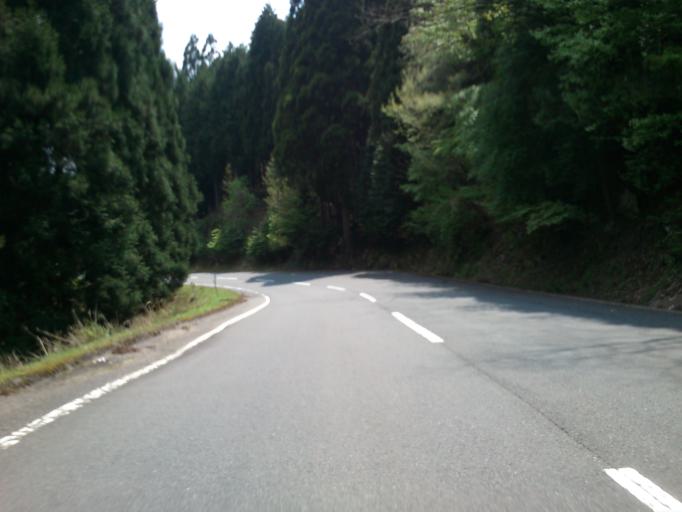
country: JP
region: Hyogo
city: Toyooka
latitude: 35.4079
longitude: 134.9501
